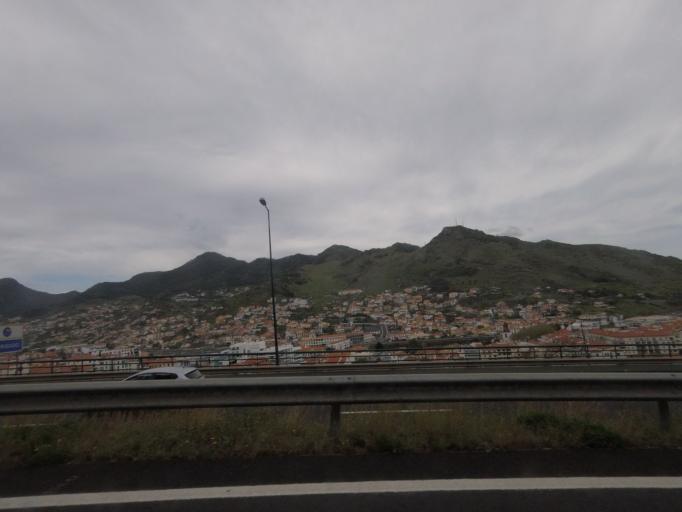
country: PT
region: Madeira
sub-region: Machico
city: Machico
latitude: 32.7168
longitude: -16.7694
